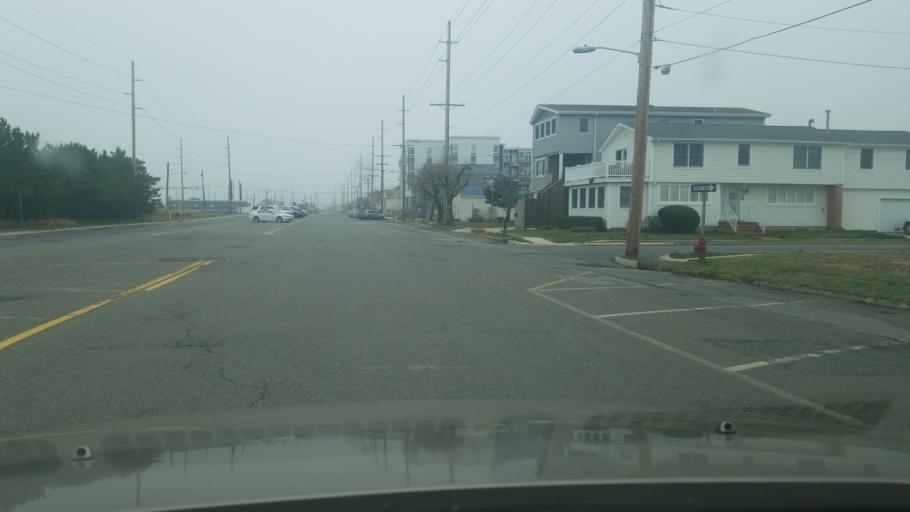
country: US
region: New Jersey
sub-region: Ocean County
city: Seaside Heights
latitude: 39.9389
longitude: -74.0798
